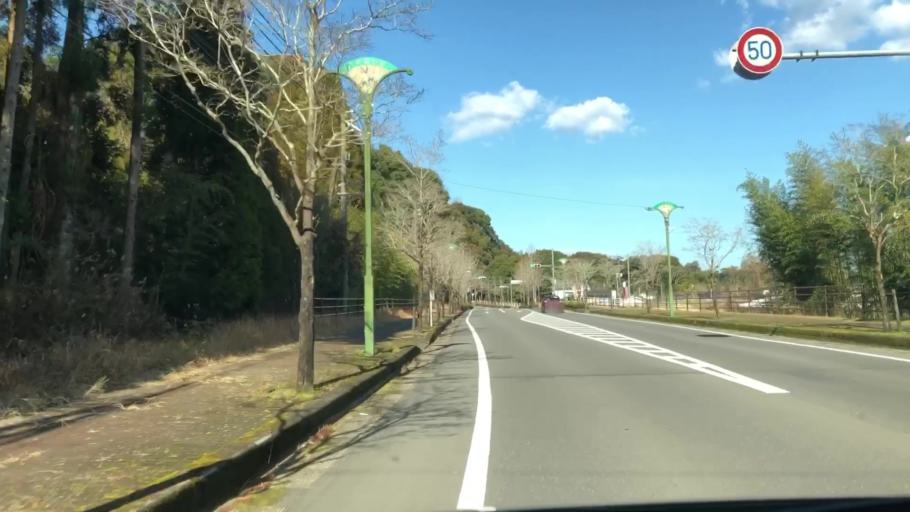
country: JP
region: Kagoshima
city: Satsumasendai
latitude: 31.8260
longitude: 130.4347
